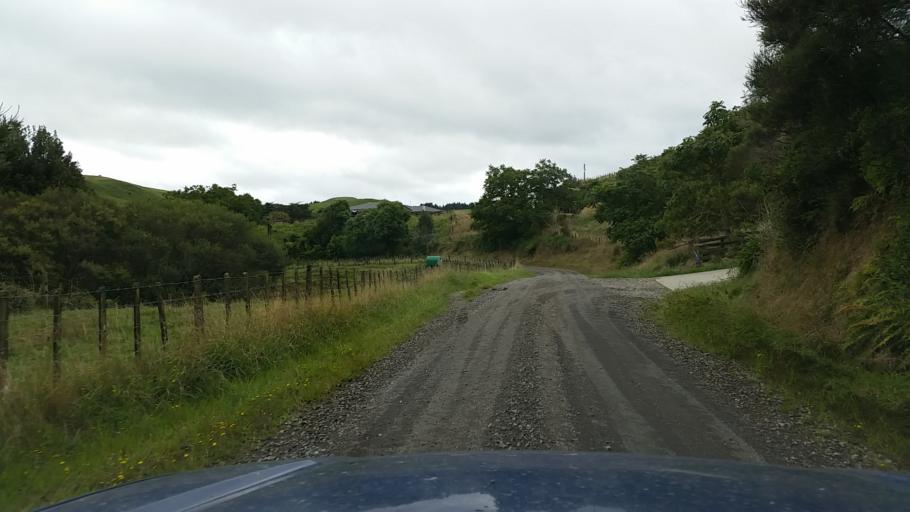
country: NZ
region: Taranaki
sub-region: South Taranaki District
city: Eltham
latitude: -39.2437
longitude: 174.3696
